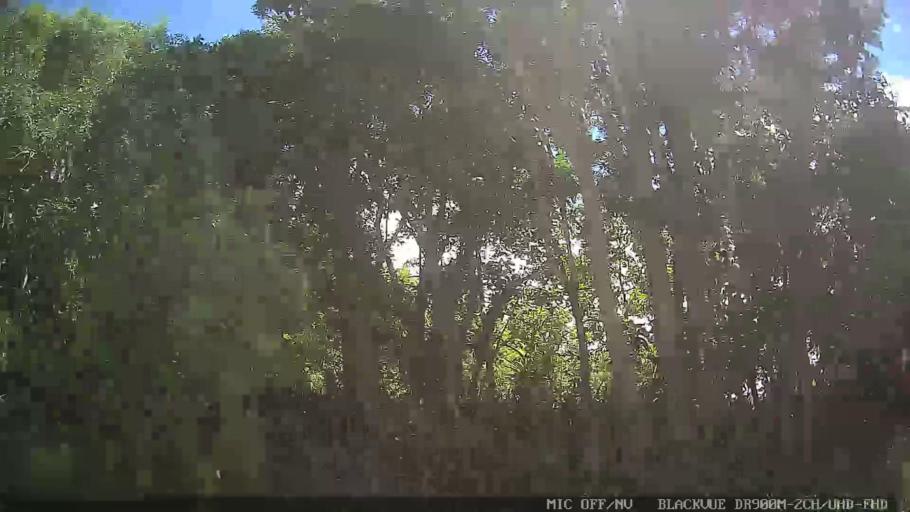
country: BR
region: Sao Paulo
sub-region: Caraguatatuba
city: Caraguatatuba
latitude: -23.5347
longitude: -45.5656
